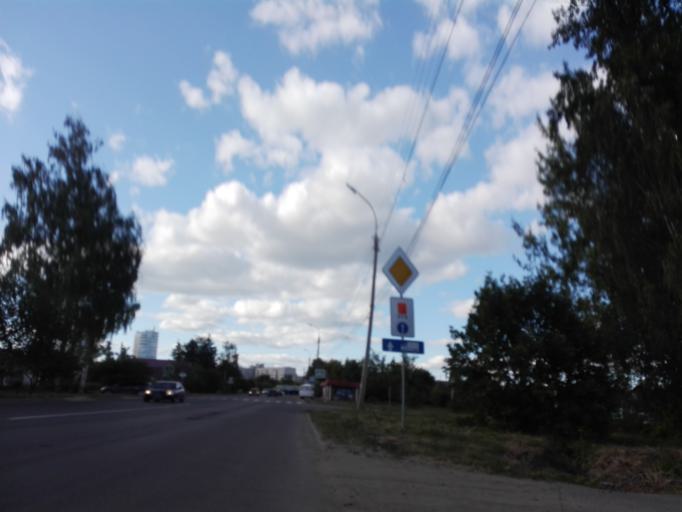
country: RU
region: Orjol
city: Orel
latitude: 52.9482
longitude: 36.0766
